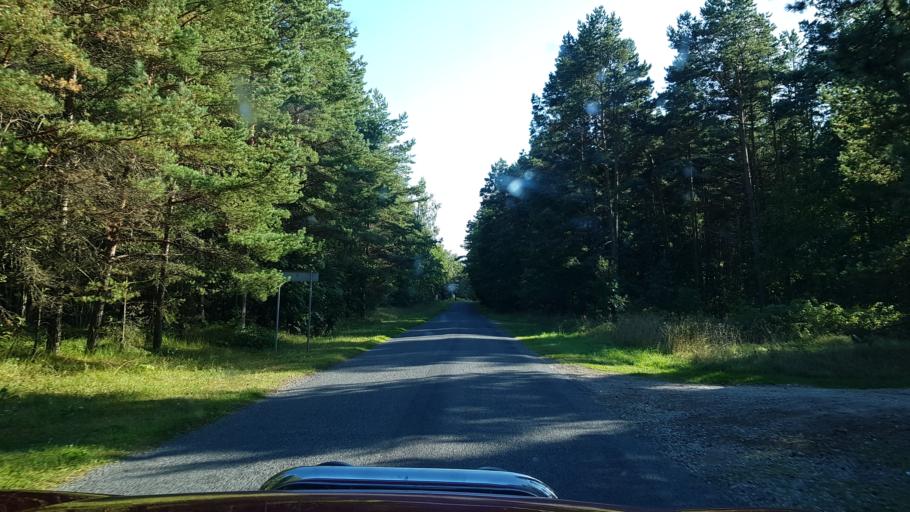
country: LV
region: Salacgrivas
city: Ainazi
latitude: 57.9168
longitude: 24.3861
